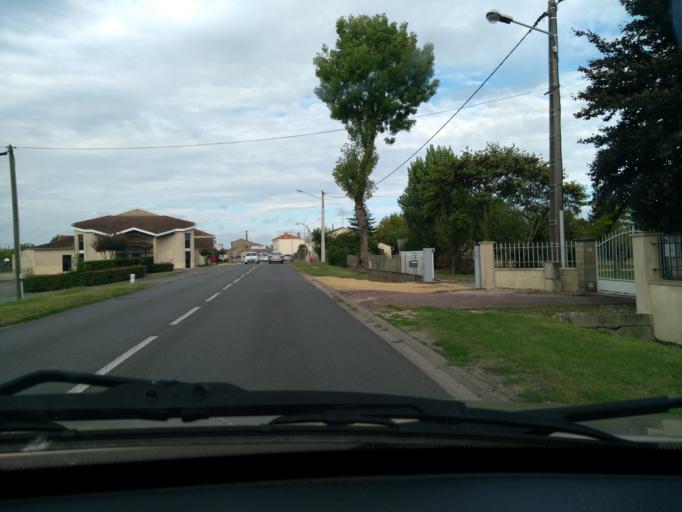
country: FR
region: Aquitaine
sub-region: Departement de la Gironde
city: Saint-Martin-Lacaussade
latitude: 45.1582
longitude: -0.6260
